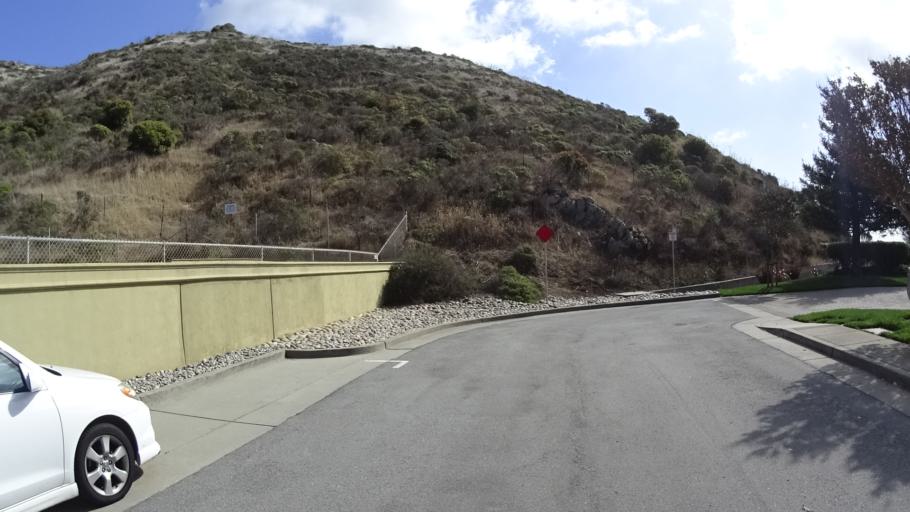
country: US
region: California
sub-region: San Mateo County
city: Brisbane
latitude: 37.6721
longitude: -122.4154
